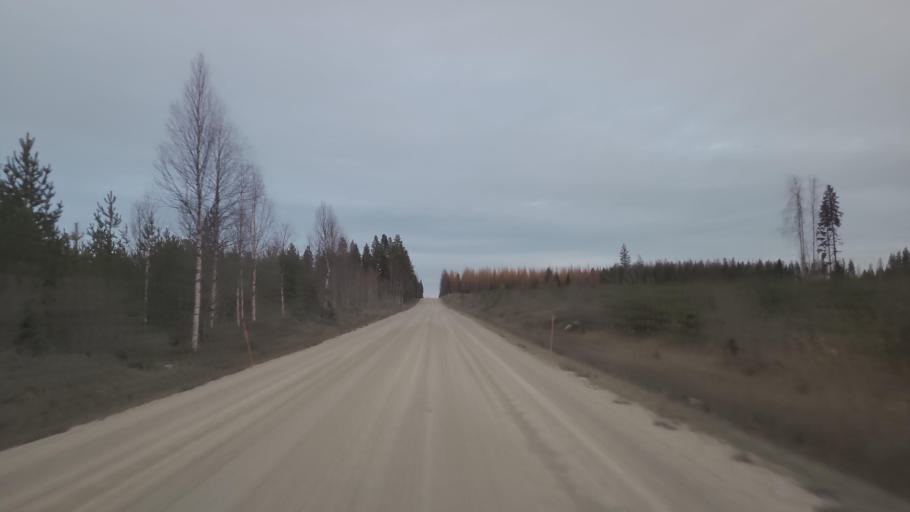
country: FI
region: Lapland
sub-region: Kemi-Tornio
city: Tervola
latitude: 66.0692
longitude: 24.8931
